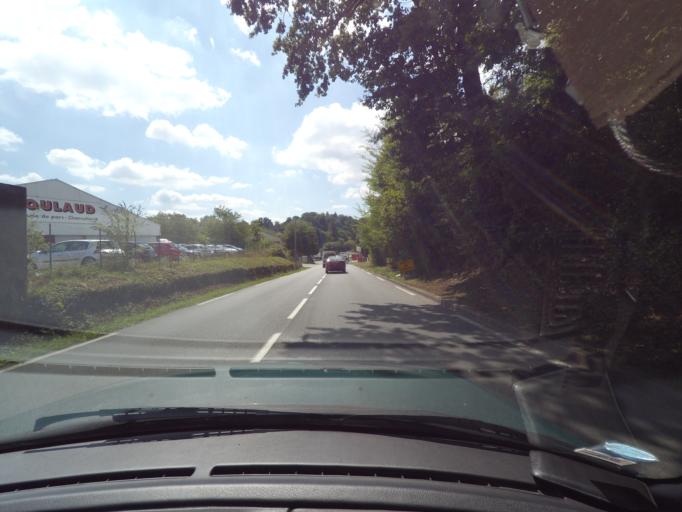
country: FR
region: Limousin
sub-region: Departement de la Haute-Vienne
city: Limoges
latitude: 45.8092
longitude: 1.2564
